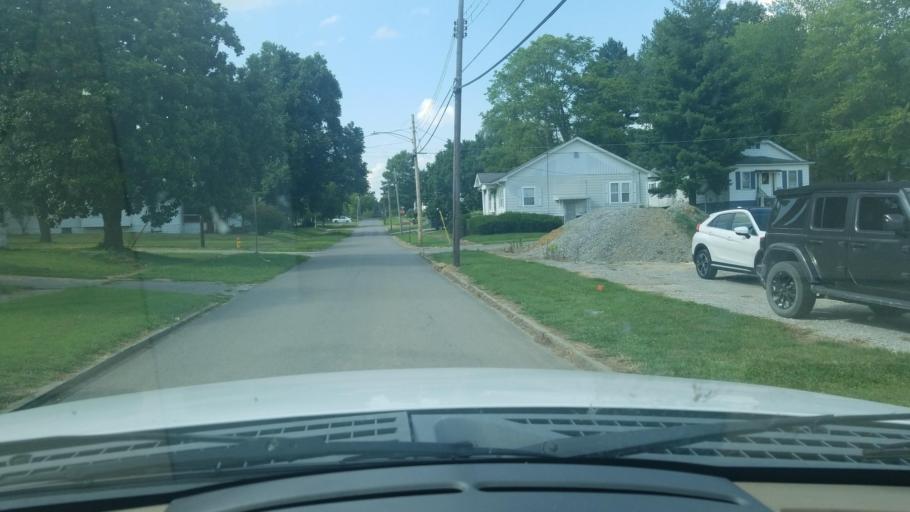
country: US
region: Illinois
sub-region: Saline County
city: Eldorado
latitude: 37.8166
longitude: -88.4430
